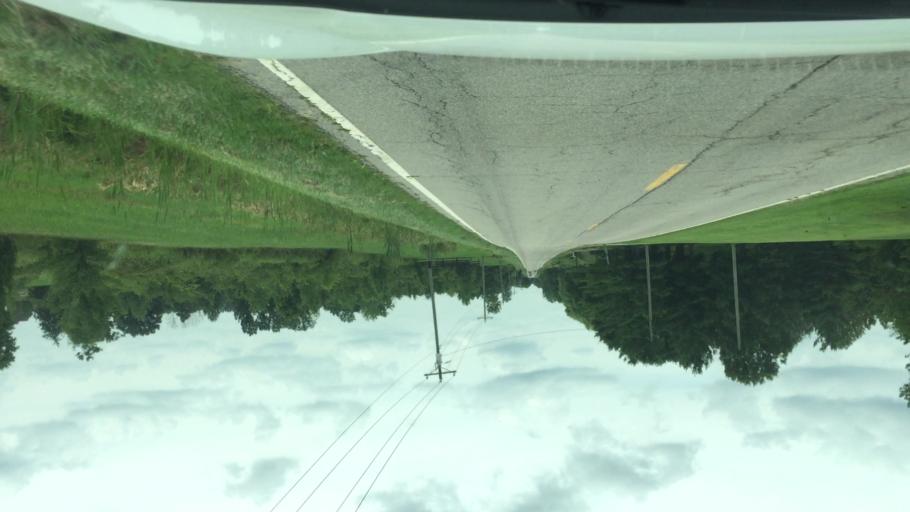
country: US
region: Ohio
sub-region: Champaign County
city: North Lewisburg
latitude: 40.2516
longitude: -83.4854
